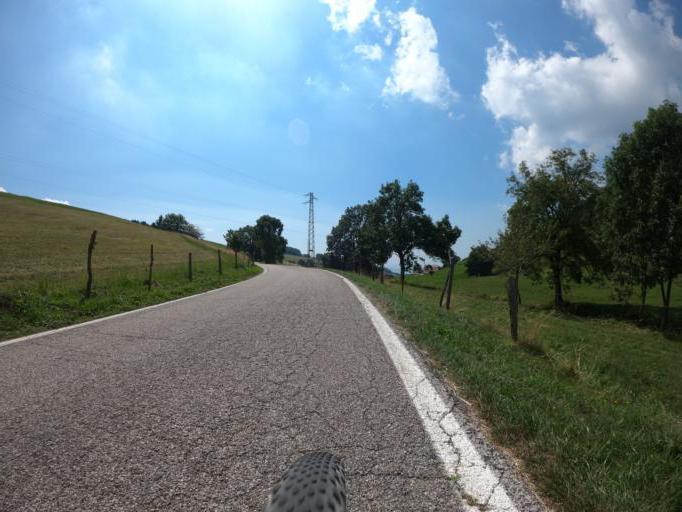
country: IT
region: Veneto
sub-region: Provincia di Verona
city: Ferrara di Monte Baldo
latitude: 45.6647
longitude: 10.8491
